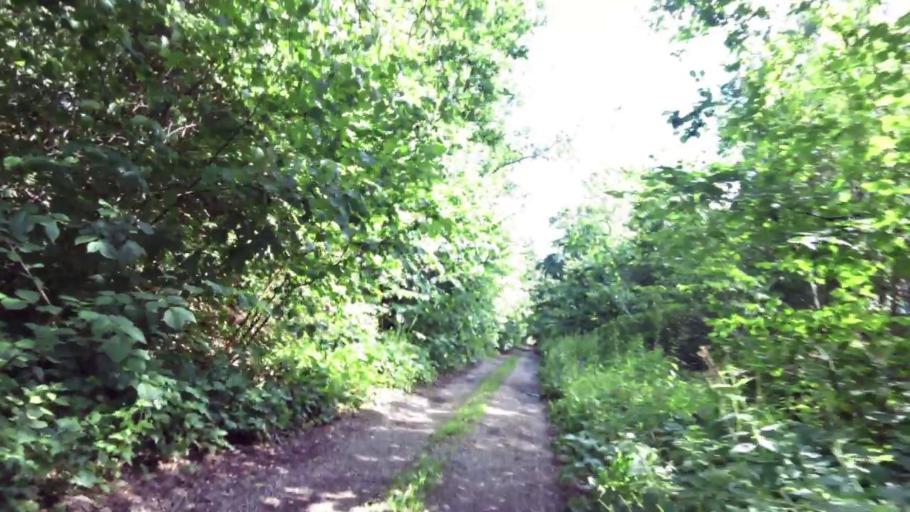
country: PL
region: West Pomeranian Voivodeship
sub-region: Powiat slawienski
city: Slawno
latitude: 54.5050
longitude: 16.7045
